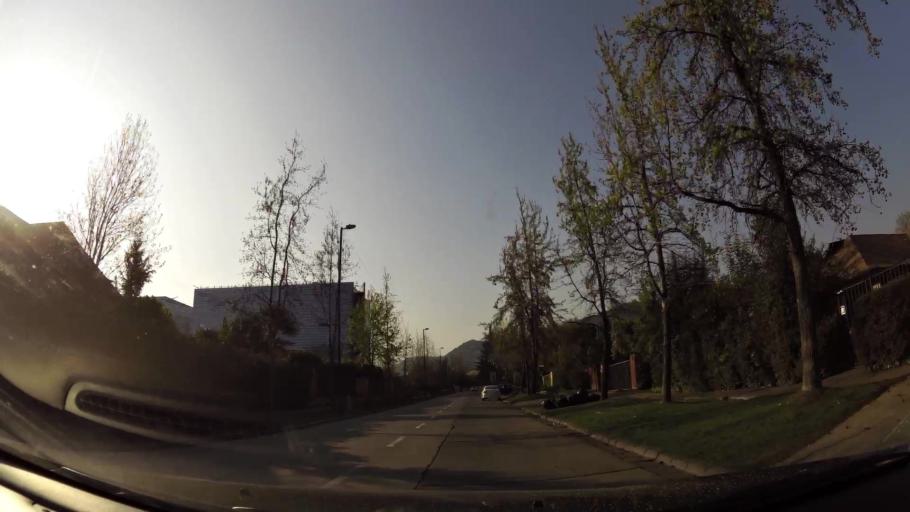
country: CL
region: Santiago Metropolitan
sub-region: Provincia de Santiago
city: Villa Presidente Frei, Nunoa, Santiago, Chile
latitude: -33.3566
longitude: -70.5344
